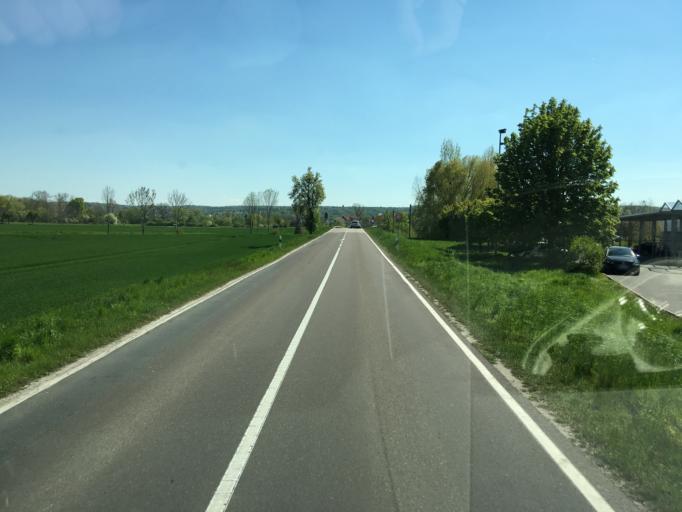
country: DE
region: Saxony-Anhalt
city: Naumburg
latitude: 51.1720
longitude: 11.7812
